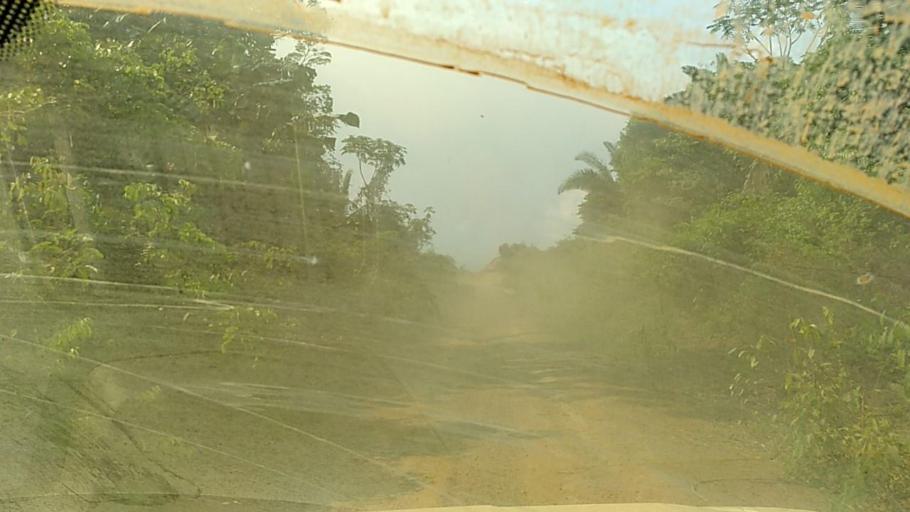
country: BR
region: Rondonia
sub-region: Porto Velho
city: Porto Velho
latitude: -8.6952
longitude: -63.2390
